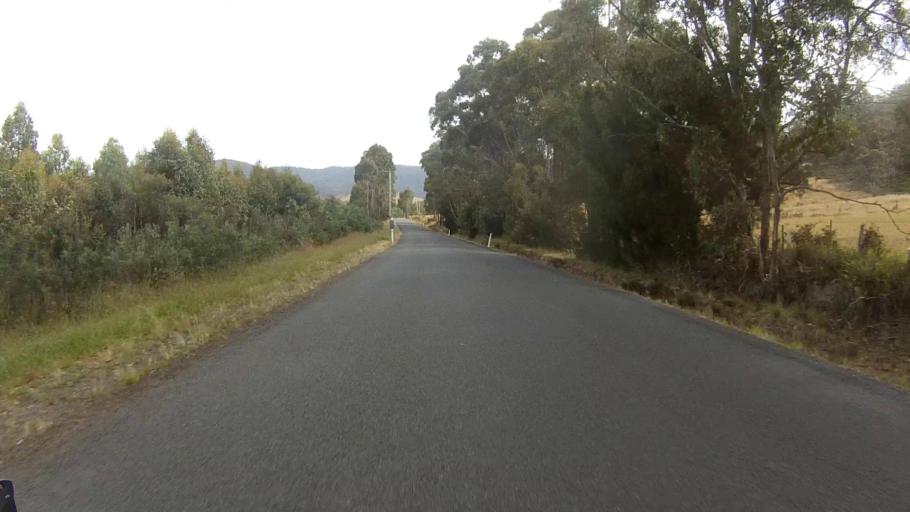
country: AU
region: Tasmania
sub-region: Sorell
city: Sorell
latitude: -42.8077
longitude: 147.7945
